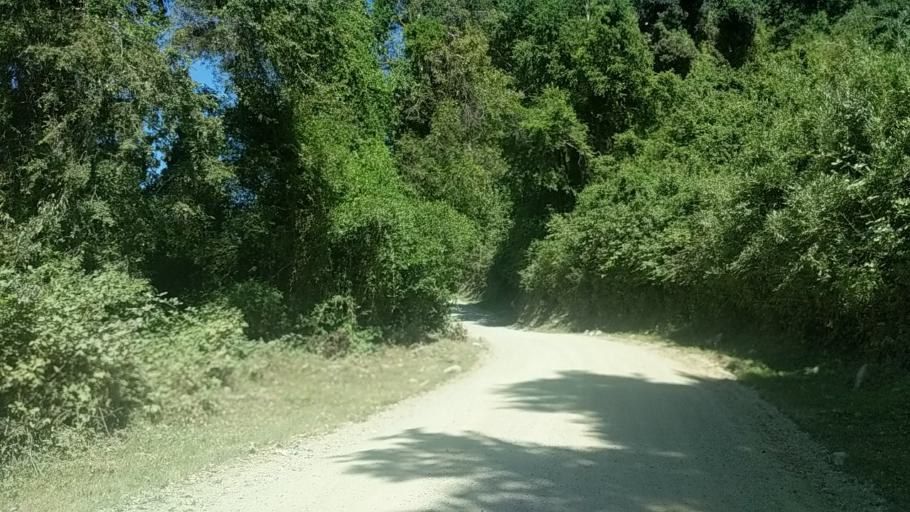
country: CL
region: Araucania
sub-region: Provincia de Cautin
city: Pucon
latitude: -39.0621
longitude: -71.7063
